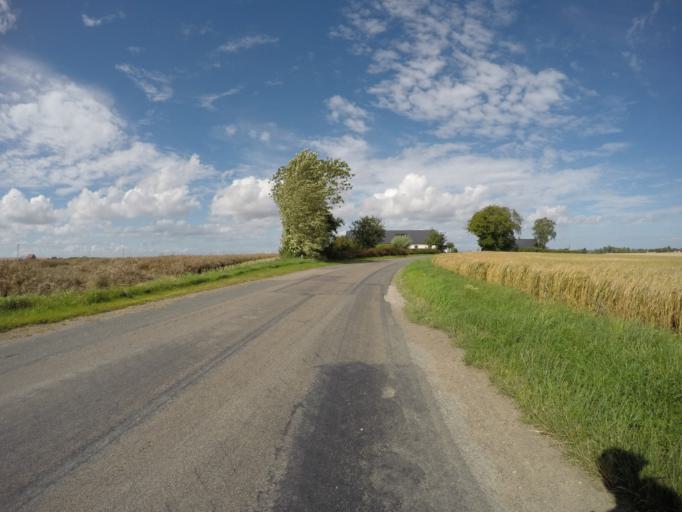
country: SE
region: Skane
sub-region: Simrishamns Kommun
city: Simrishamn
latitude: 55.4908
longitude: 14.1946
